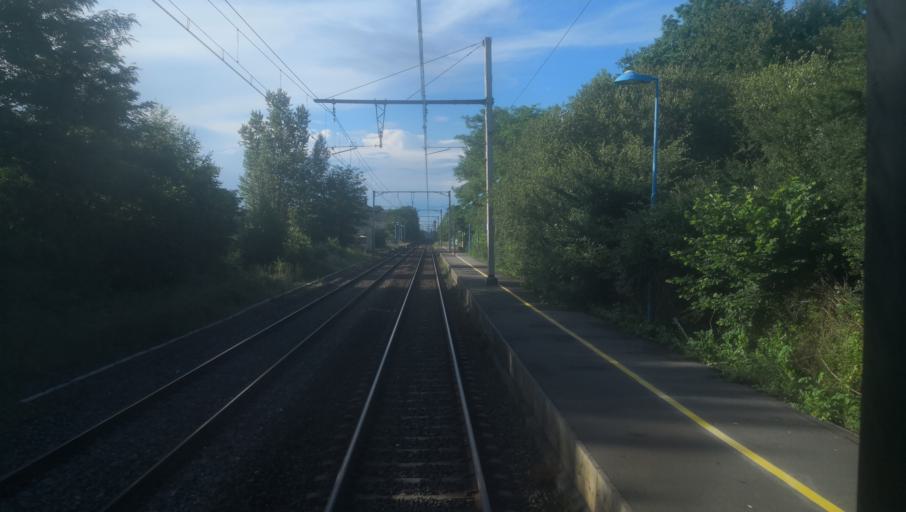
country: FR
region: Centre
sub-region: Departement du Loir-et-Cher
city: Theillay
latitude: 47.3133
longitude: 2.0444
